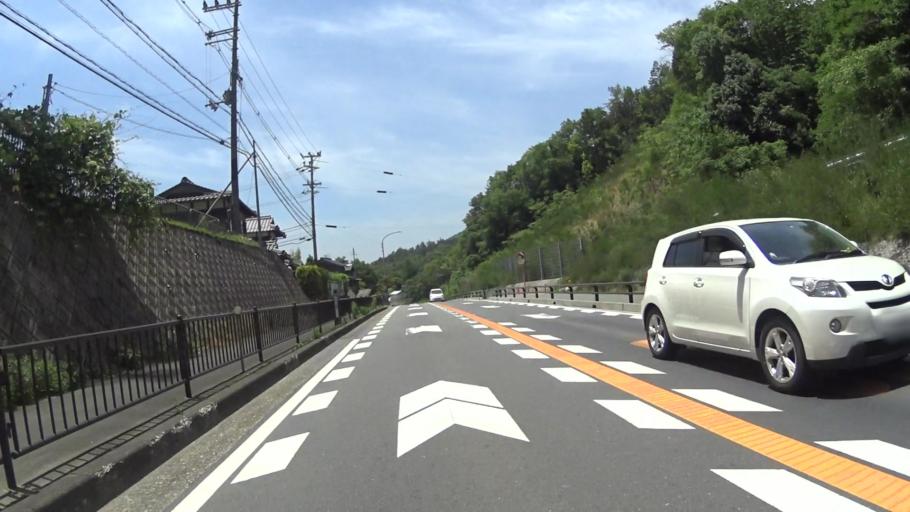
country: JP
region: Kyoto
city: Ayabe
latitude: 35.1884
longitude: 135.3210
